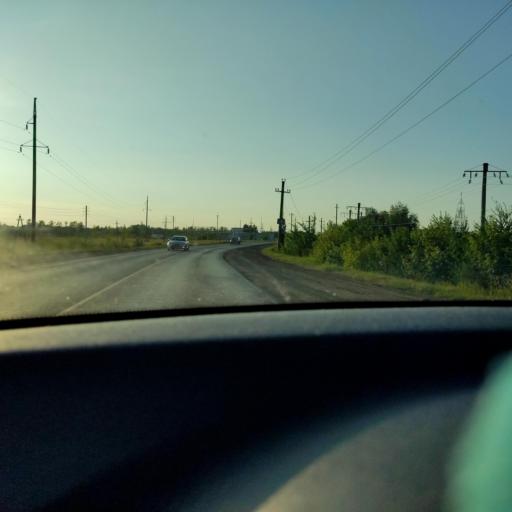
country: RU
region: Samara
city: Kinel'
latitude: 53.2363
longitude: 50.5818
